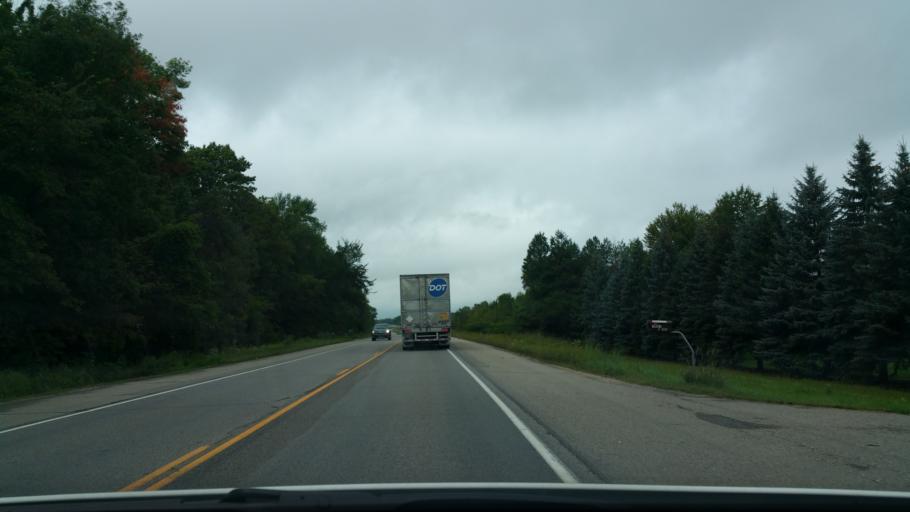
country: US
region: Minnesota
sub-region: Rice County
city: Dundas
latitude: 44.4720
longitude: -93.2800
